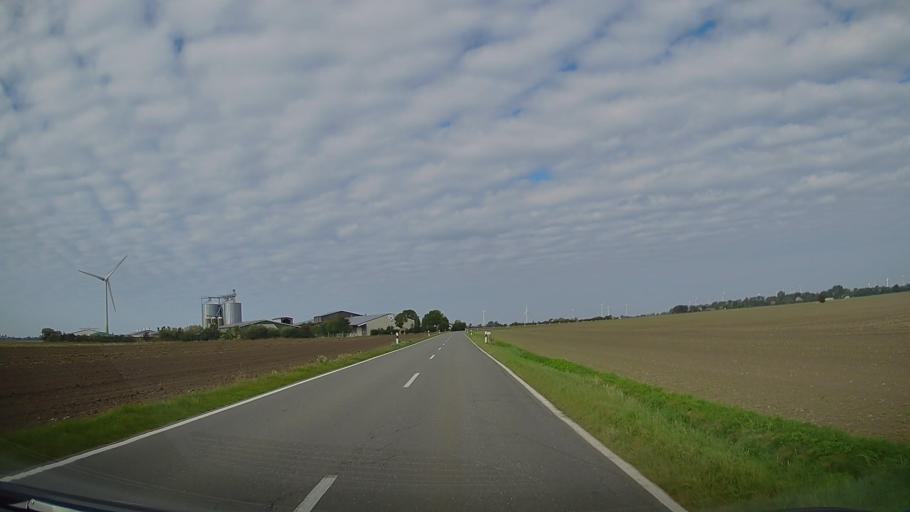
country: DE
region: Schleswig-Holstein
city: Grossenbrode
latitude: 54.4856
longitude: 11.0643
